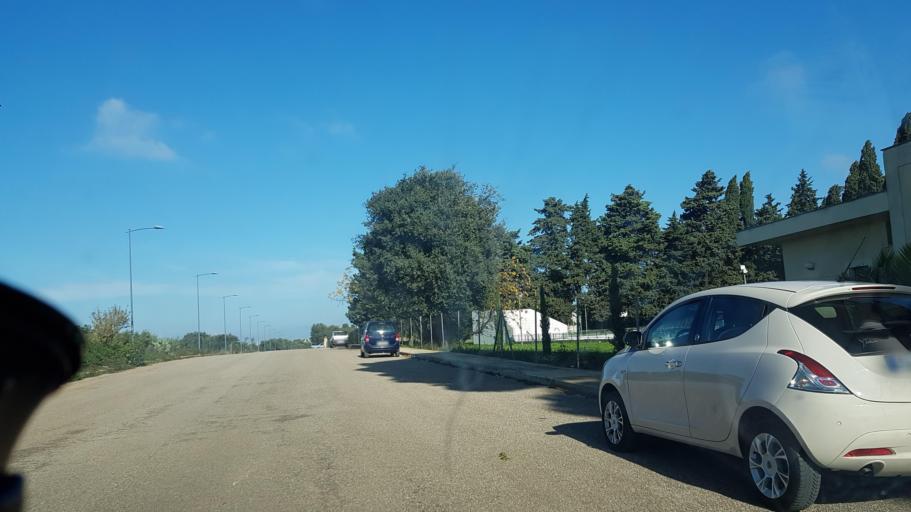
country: IT
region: Apulia
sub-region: Provincia di Brindisi
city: Carovigno
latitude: 40.7099
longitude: 17.6541
